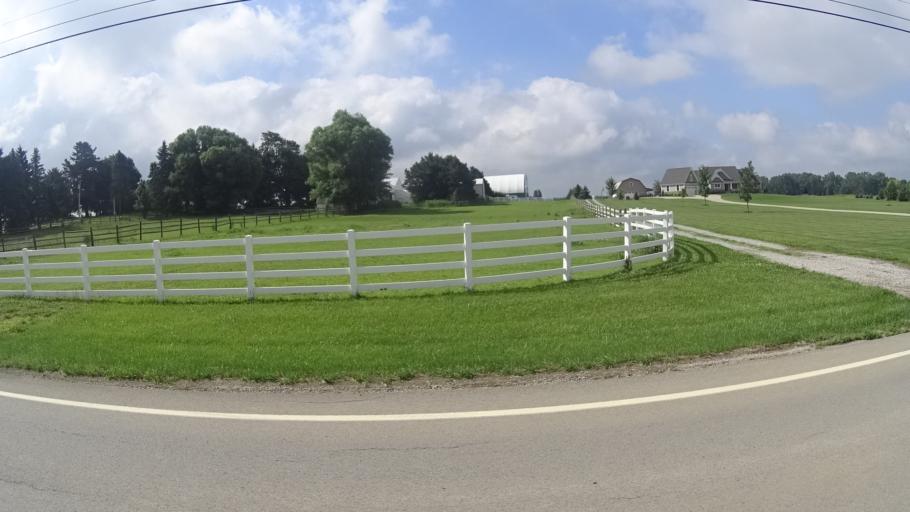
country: US
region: Ohio
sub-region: Huron County
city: Wakeman
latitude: 41.3078
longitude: -82.4558
